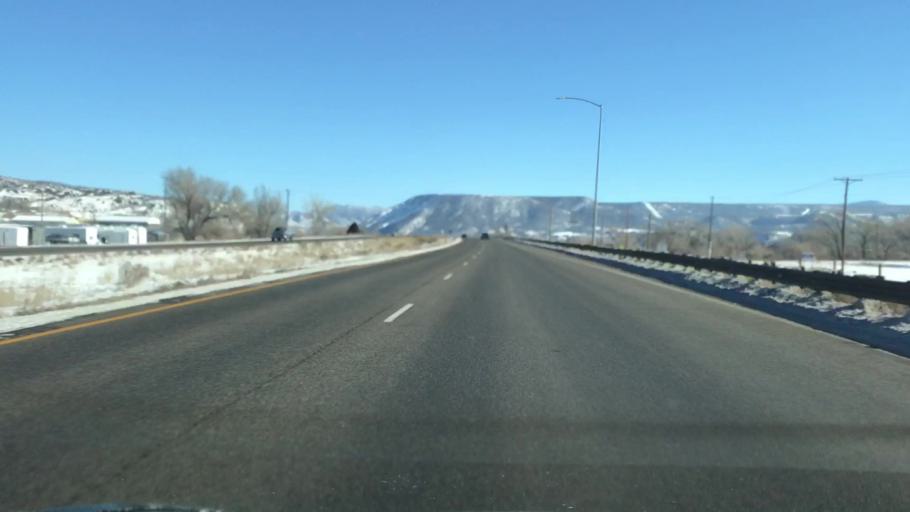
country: US
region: Colorado
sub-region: Garfield County
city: Silt
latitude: 39.5444
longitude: -107.6483
